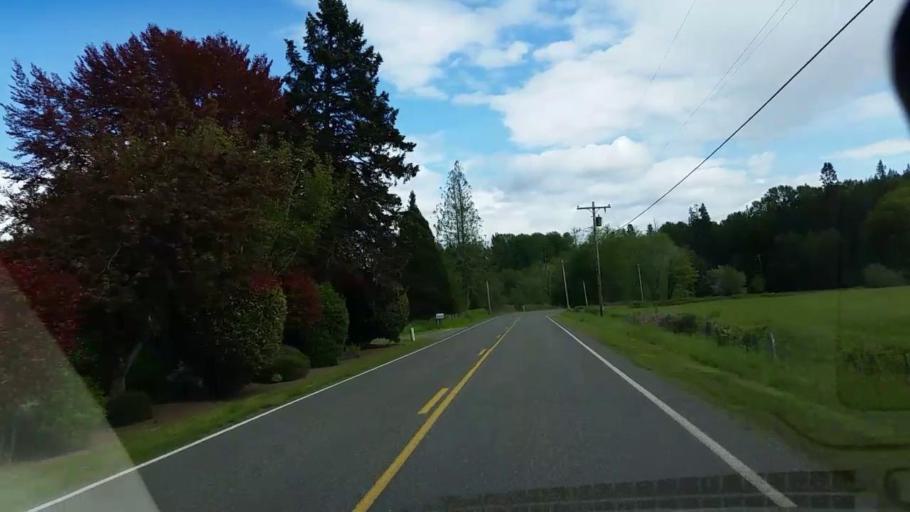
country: US
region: Washington
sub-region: Mason County
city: Shelton
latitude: 47.3181
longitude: -123.2592
